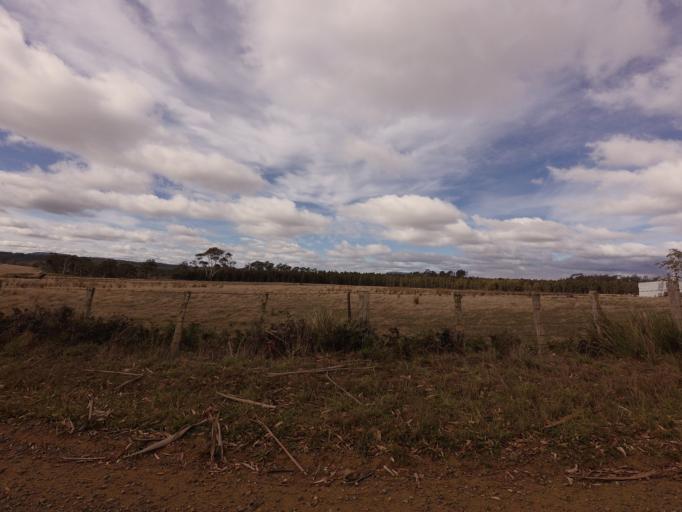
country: AU
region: Tasmania
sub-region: Brighton
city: Bridgewater
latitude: -42.4394
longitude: 147.3858
